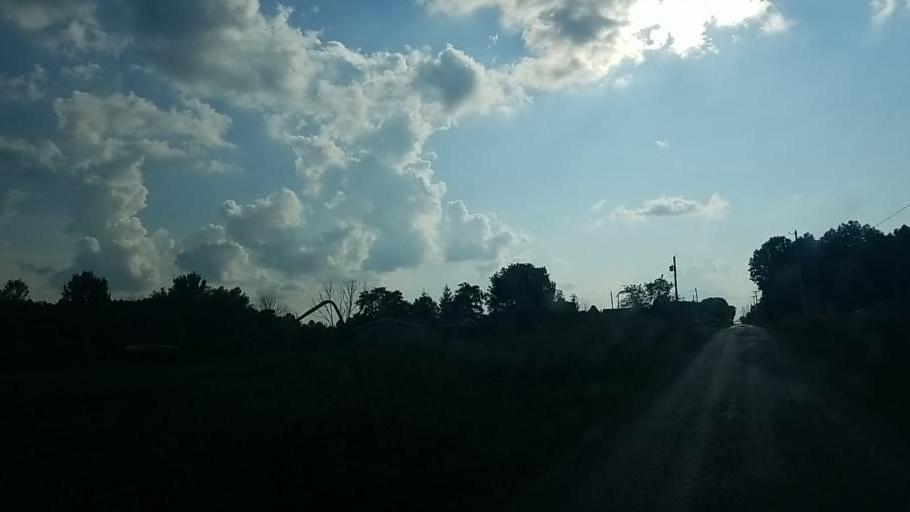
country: US
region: Ohio
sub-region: Wayne County
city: West Salem
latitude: 40.9049
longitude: -82.1921
